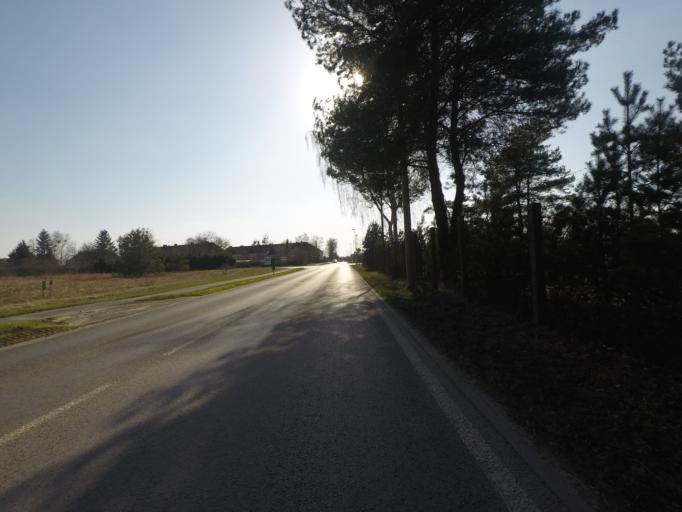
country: DE
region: Brandenburg
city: Eberswalde
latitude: 52.8469
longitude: 13.7469
